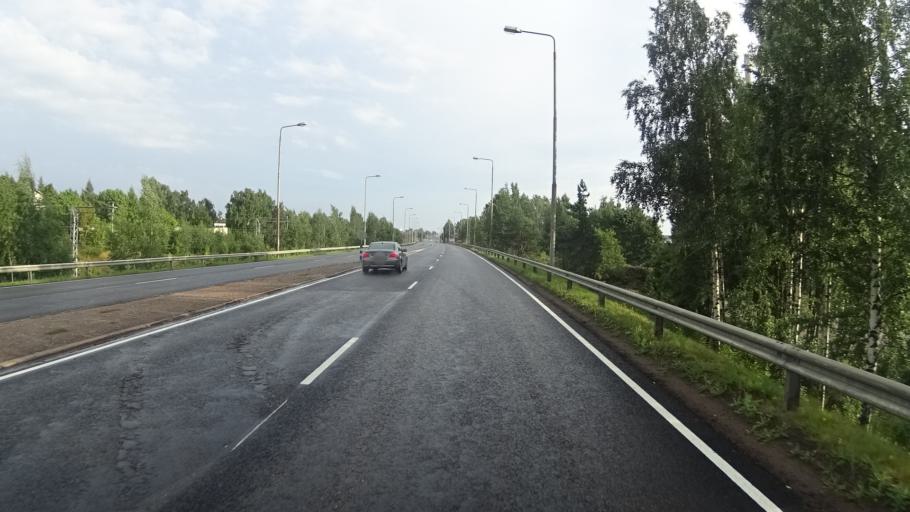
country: FI
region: Kymenlaakso
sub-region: Kotka-Hamina
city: Kotka
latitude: 60.4726
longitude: 26.9178
